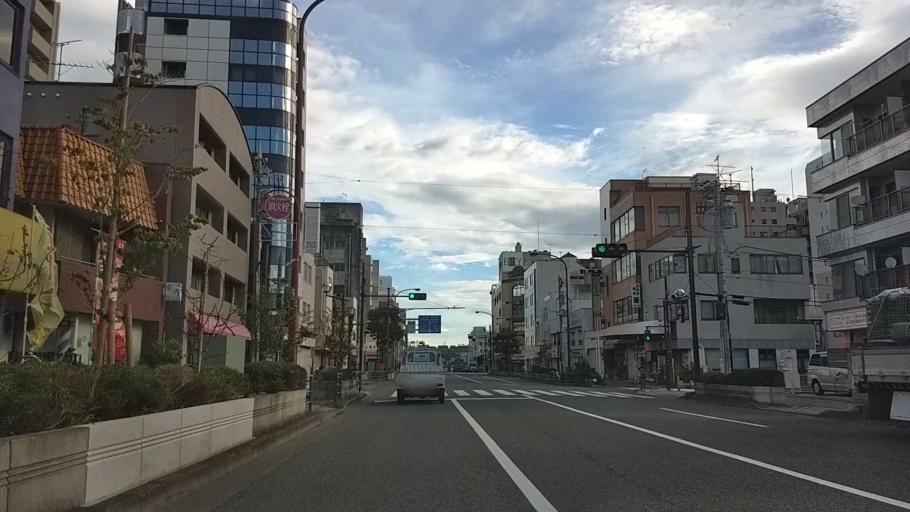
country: JP
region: Tokyo
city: Hachioji
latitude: 35.6592
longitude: 139.3285
